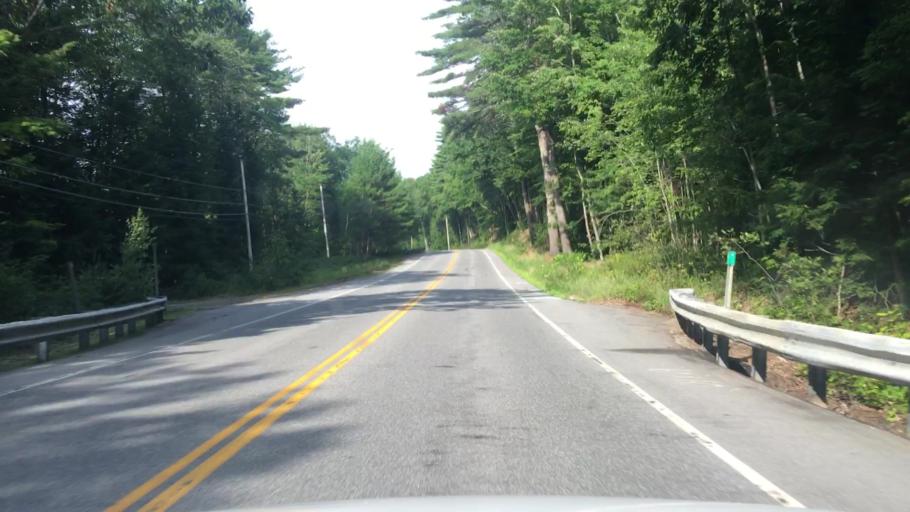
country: US
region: Maine
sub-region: Oxford County
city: Porter
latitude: 43.8019
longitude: -70.9115
